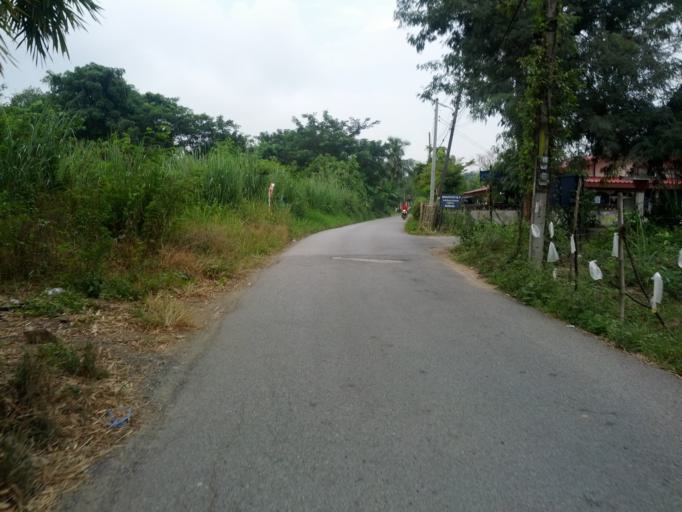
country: TH
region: Chiang Mai
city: San Kamphaeng
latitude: 18.7569
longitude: 99.1229
